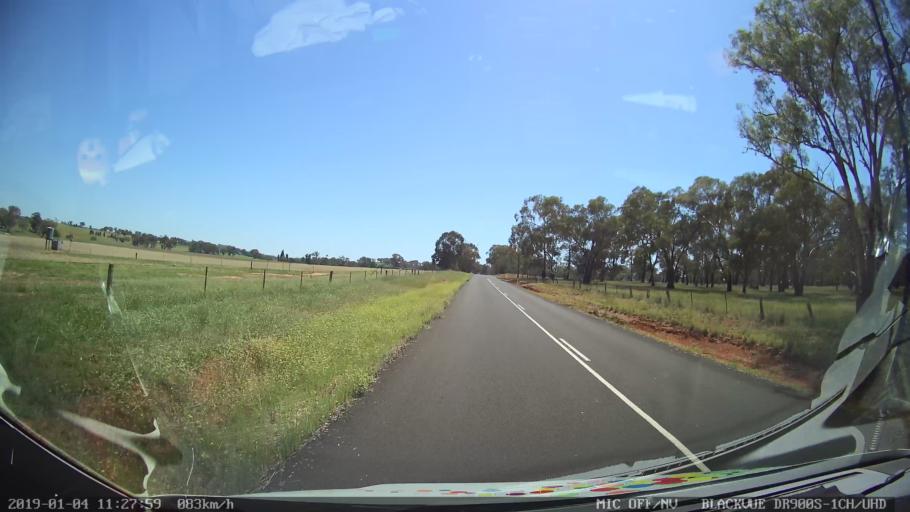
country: AU
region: New South Wales
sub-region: Cabonne
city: Molong
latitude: -33.1041
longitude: 148.7678
